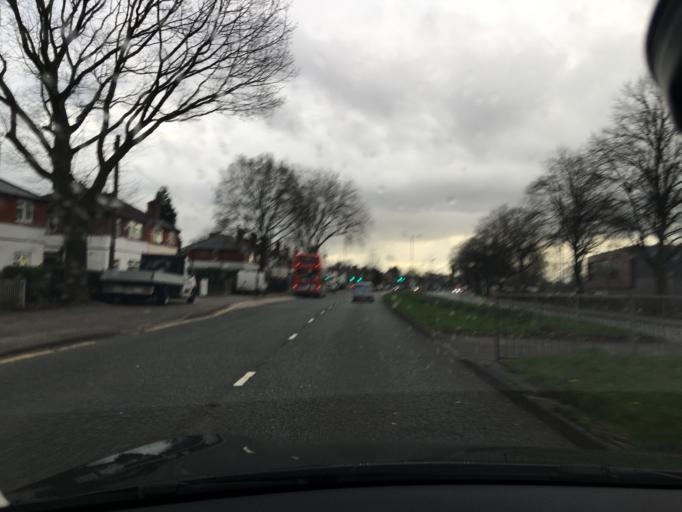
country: GB
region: England
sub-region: Manchester
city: Chorlton cum Hardy
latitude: 53.4371
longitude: -2.2445
